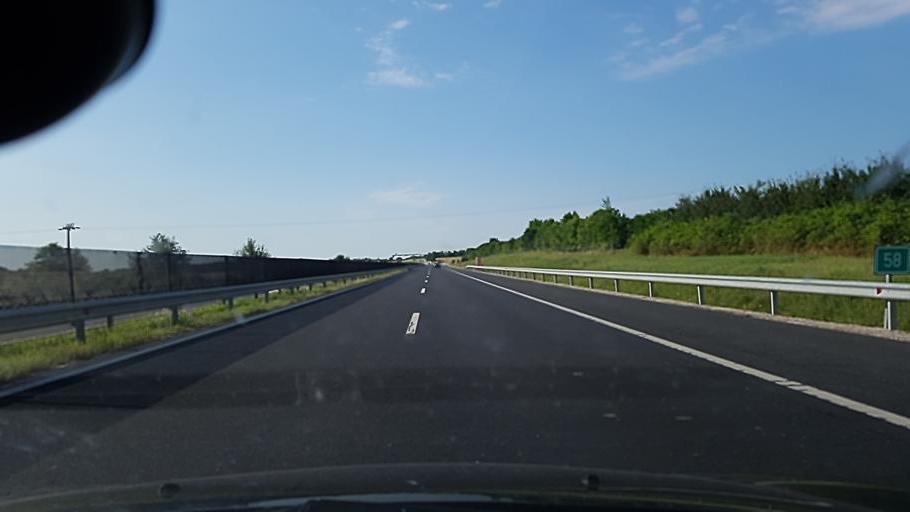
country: HU
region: Fejer
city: Adony
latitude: 47.0658
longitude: 18.8816
